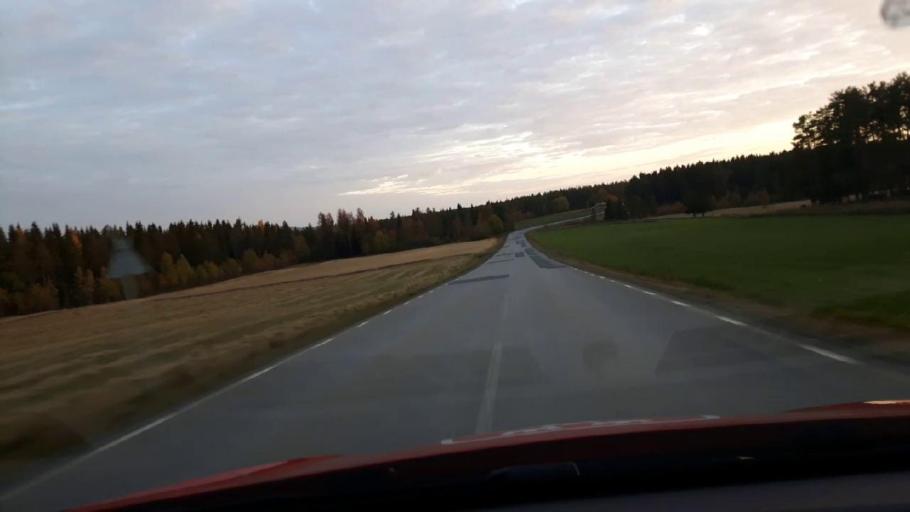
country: SE
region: Jaemtland
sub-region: OEstersunds Kommun
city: Ostersund
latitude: 63.2544
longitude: 14.6062
